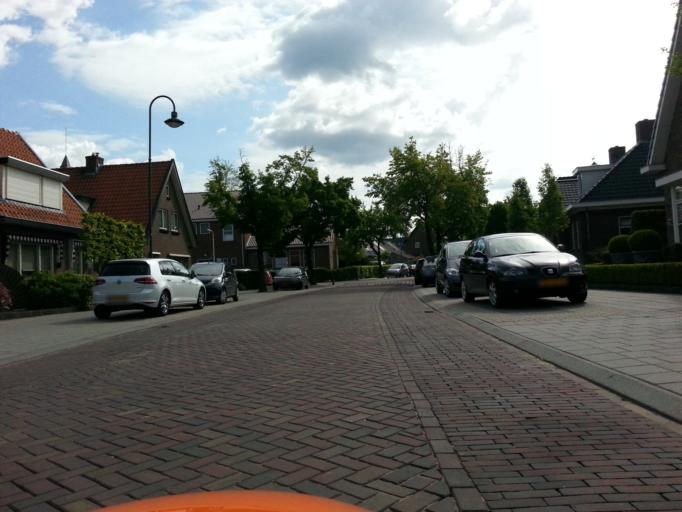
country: NL
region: Gelderland
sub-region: Gemeente Ede
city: Lunteren
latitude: 52.0868
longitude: 5.6150
